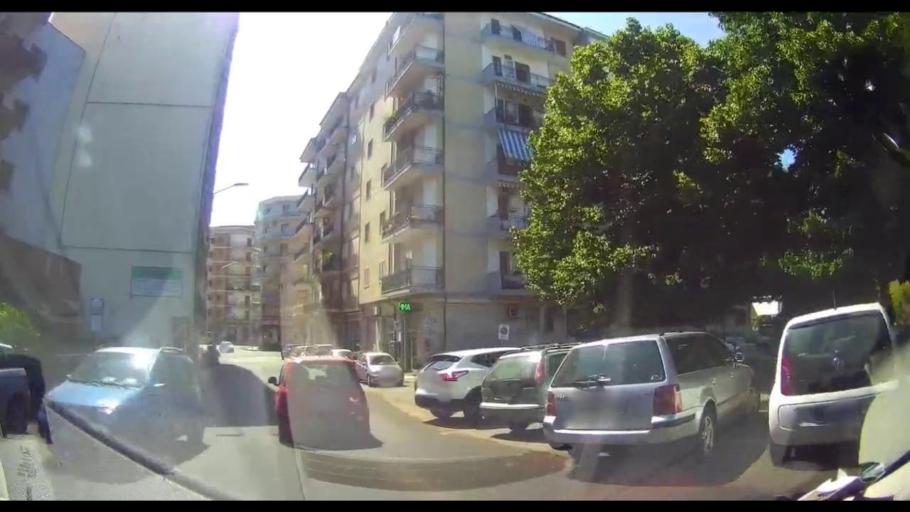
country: IT
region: Calabria
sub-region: Provincia di Cosenza
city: Cosenza
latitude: 39.3092
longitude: 16.2511
